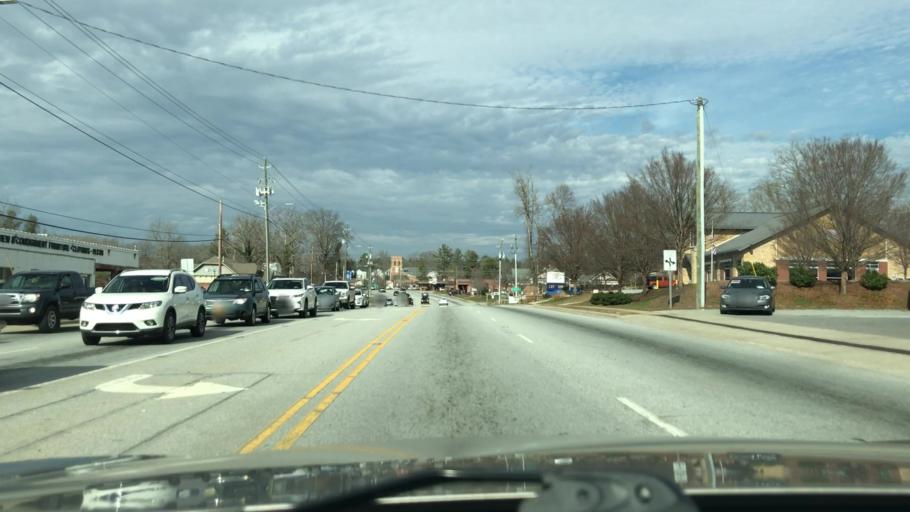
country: US
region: North Carolina
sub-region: Henderson County
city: Fletcher
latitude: 35.4311
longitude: -82.5013
